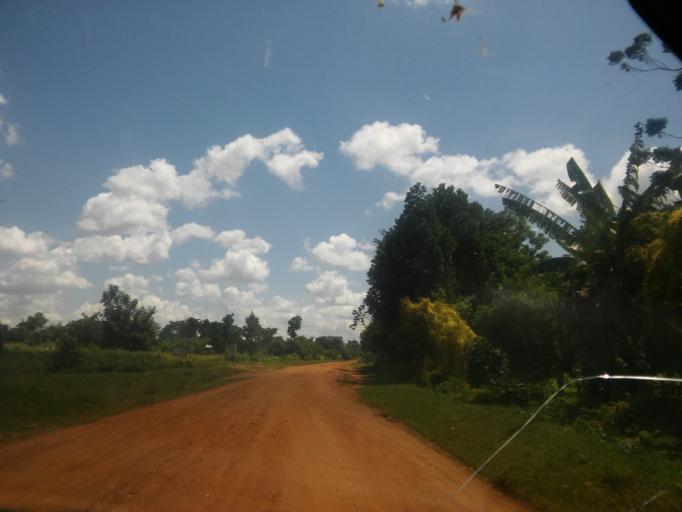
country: UG
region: Eastern Region
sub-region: Budaka District
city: Budaka
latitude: 1.1120
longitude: 33.9580
